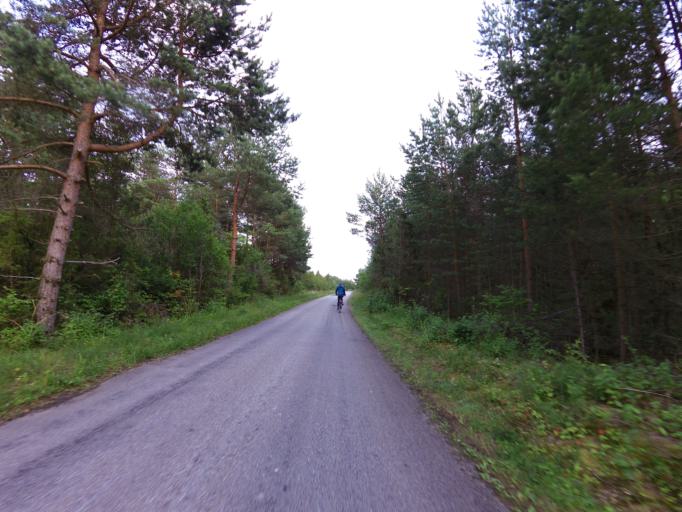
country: EE
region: Laeaene
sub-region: Vormsi vald
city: Hullo
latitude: 58.9753
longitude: 23.2595
